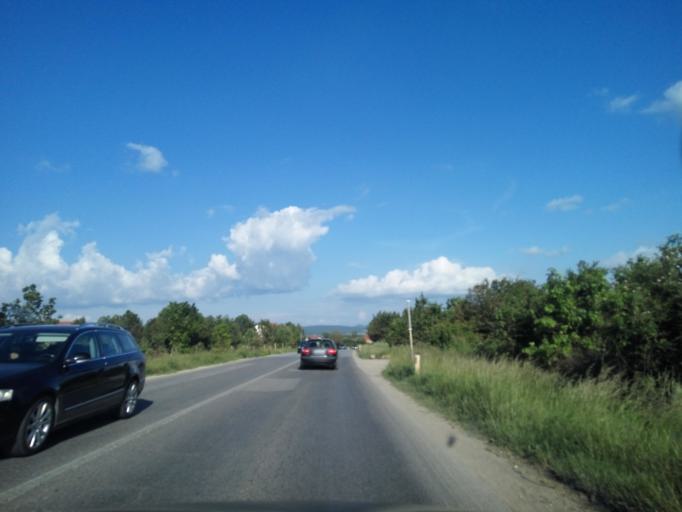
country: XK
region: Prizren
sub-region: Komuna e Malisheves
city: Llazice
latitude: 42.5868
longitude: 20.6831
